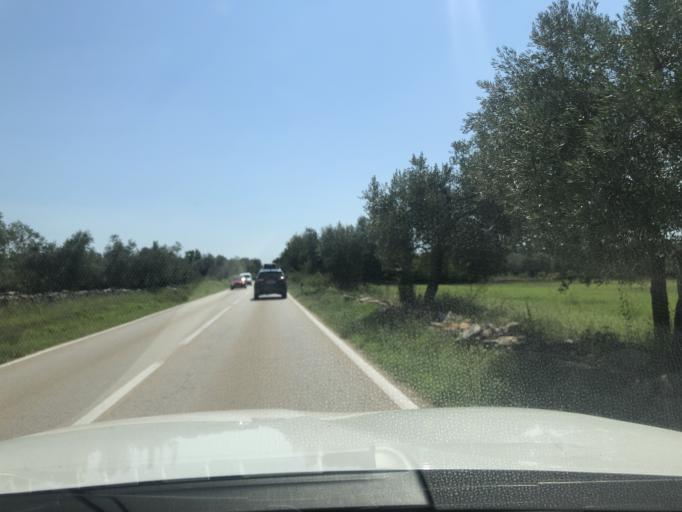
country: HR
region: Istarska
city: Vodnjan
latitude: 45.0247
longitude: 13.8000
